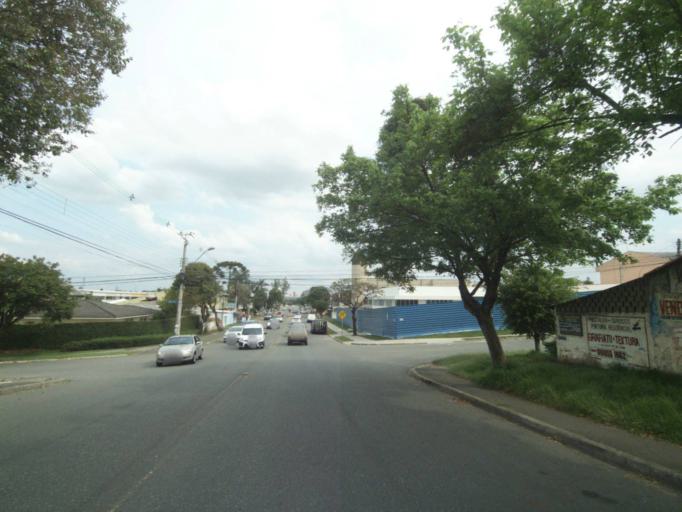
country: BR
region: Parana
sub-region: Pinhais
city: Pinhais
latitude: -25.4217
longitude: -49.2020
